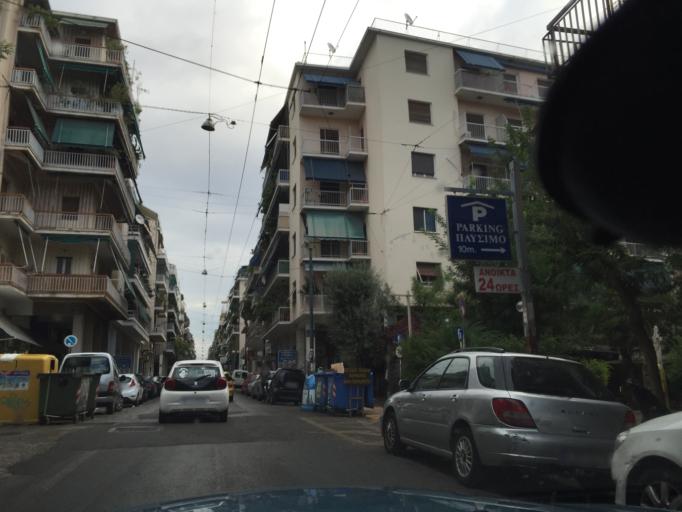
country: GR
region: Attica
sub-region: Nomarchia Athinas
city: Athens
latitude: 37.9630
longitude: 23.7216
